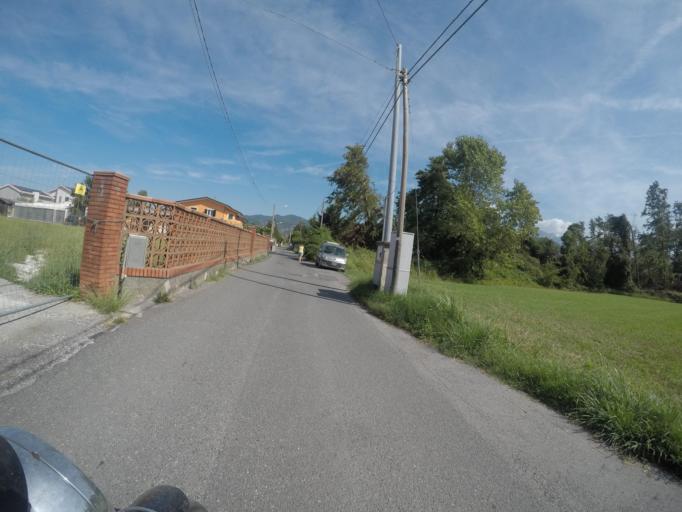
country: IT
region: Liguria
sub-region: Provincia di La Spezia
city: Casano-Dogana-Isola
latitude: 44.0561
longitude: 10.0320
